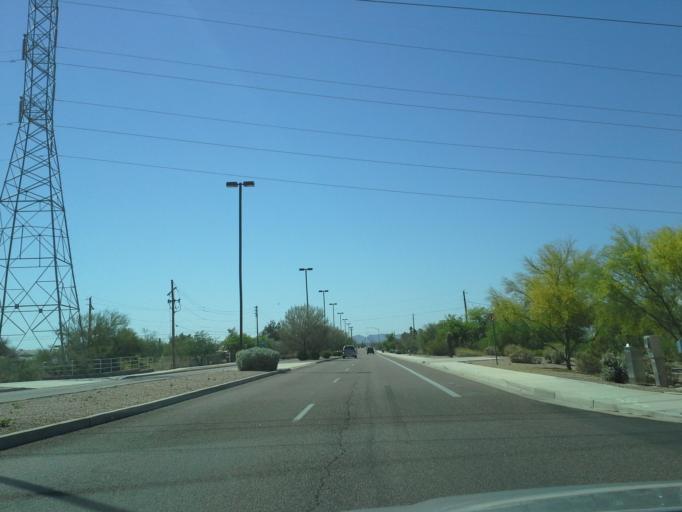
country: US
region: Arizona
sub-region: Pinal County
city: Apache Junction
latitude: 33.4333
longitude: -111.6328
